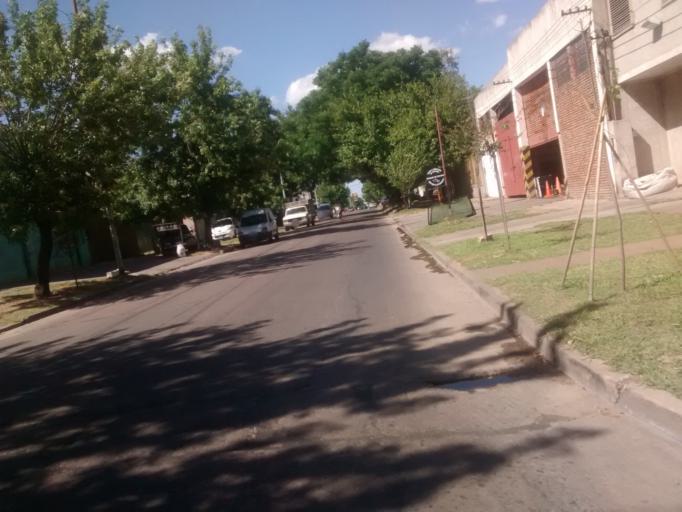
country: AR
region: Buenos Aires
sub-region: Partido de La Plata
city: La Plata
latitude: -34.9305
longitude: -57.9122
